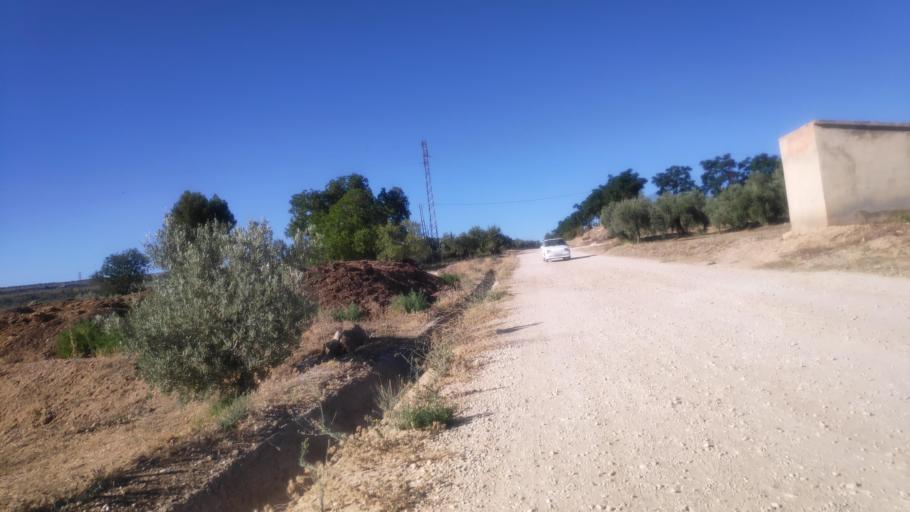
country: ES
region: Andalusia
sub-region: Provincia de Jaen
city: Pozo Alcon
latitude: 37.6680
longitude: -2.9720
